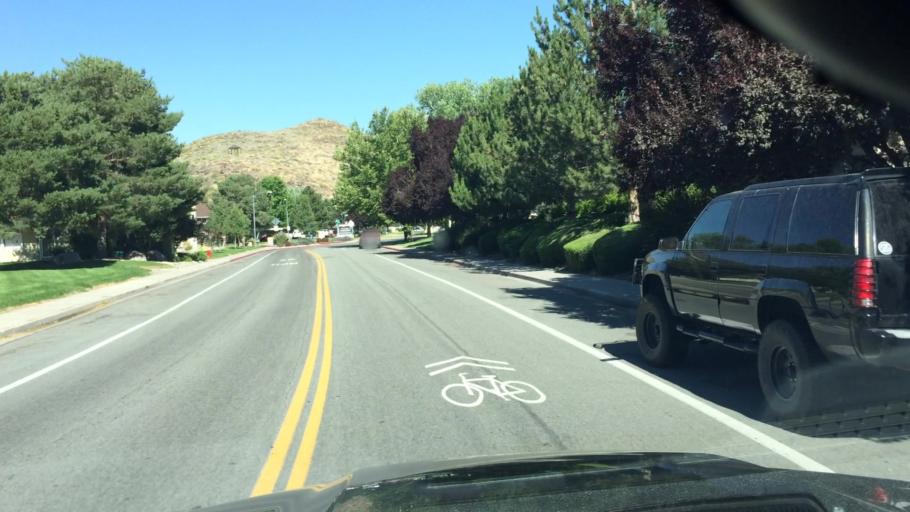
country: US
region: Nevada
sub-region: Washoe County
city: Sparks
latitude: 39.4535
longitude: -119.7729
